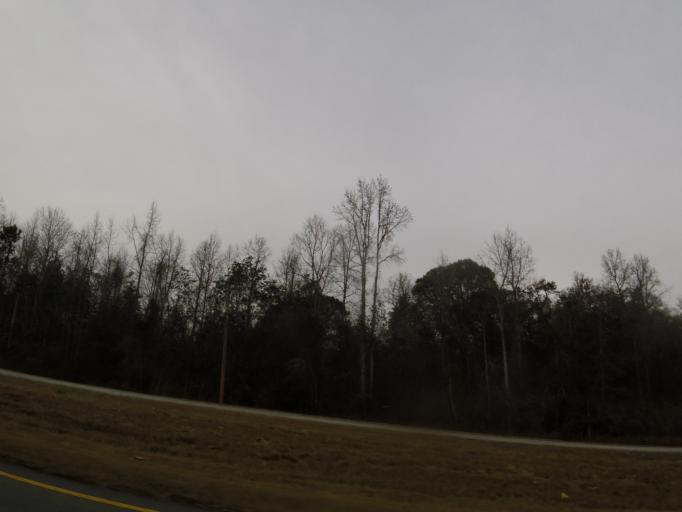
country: US
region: Georgia
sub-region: Thomas County
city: Thomasville
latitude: 30.8778
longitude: -84.0564
